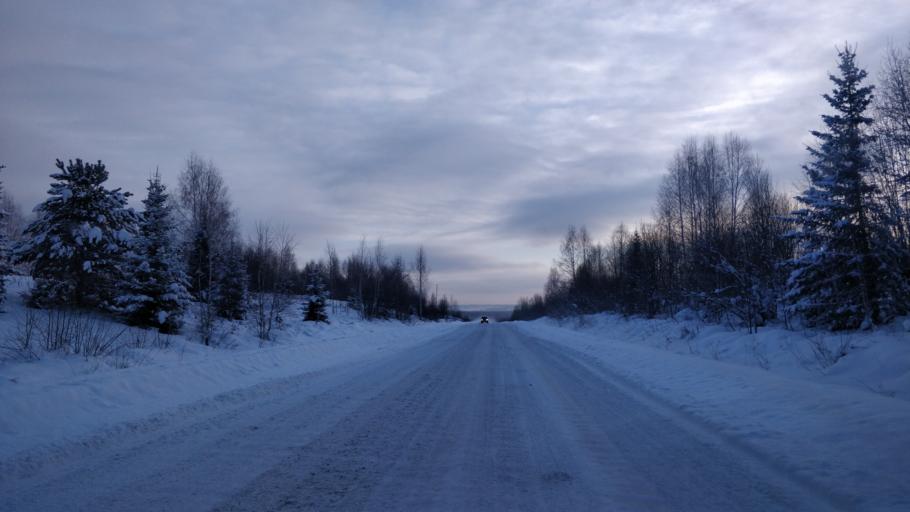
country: RU
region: Perm
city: Verkhnechusovskiye Gorodki
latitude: 58.2123
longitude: 57.1416
